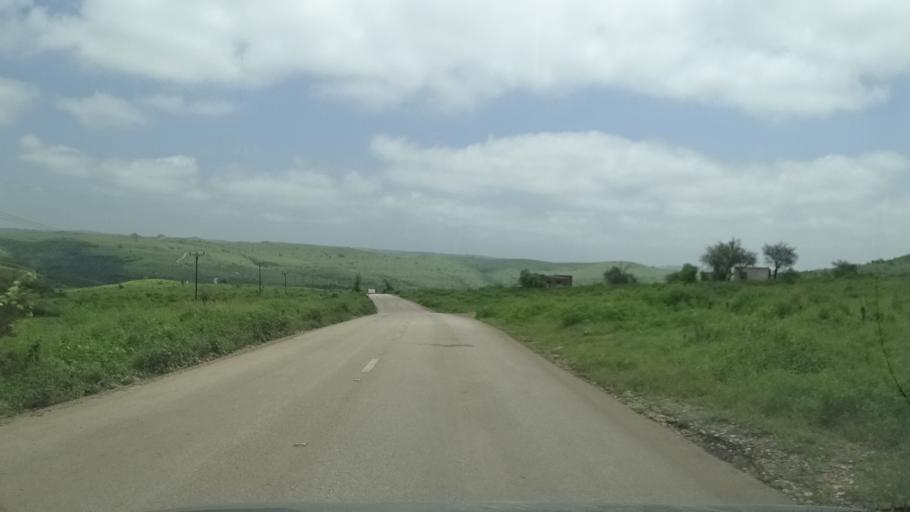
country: OM
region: Zufar
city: Salalah
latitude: 17.1947
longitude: 54.1691
